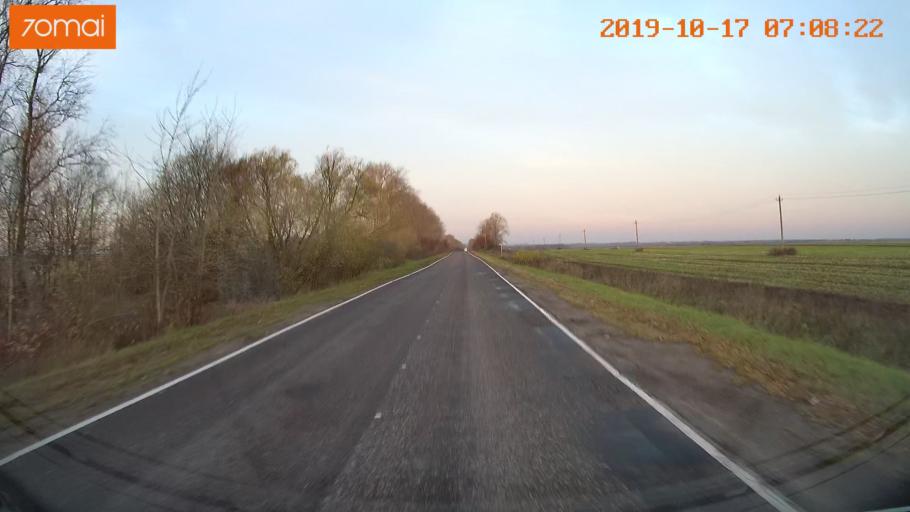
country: RU
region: Vladimir
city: Suzdal'
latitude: 56.4231
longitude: 40.4079
